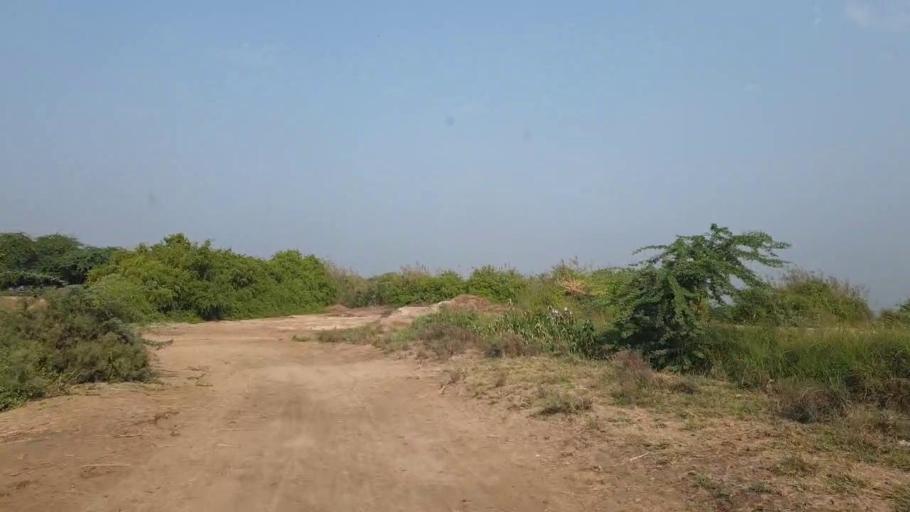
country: PK
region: Sindh
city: Talhar
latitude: 24.8420
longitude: 68.7996
